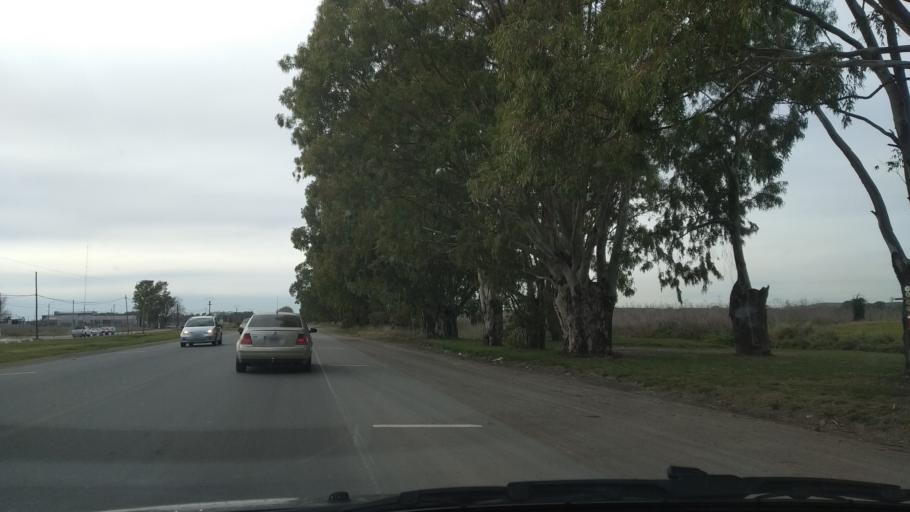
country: AR
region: Buenos Aires
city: Olavarria
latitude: -36.9749
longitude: -60.2784
